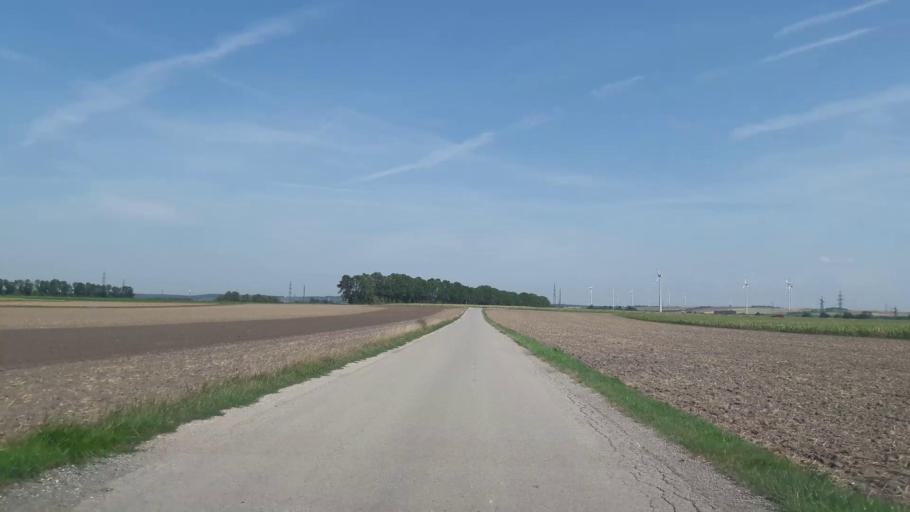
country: AT
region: Lower Austria
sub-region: Politischer Bezirk Bruck an der Leitha
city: Bruck an der Leitha
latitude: 48.0248
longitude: 16.7605
